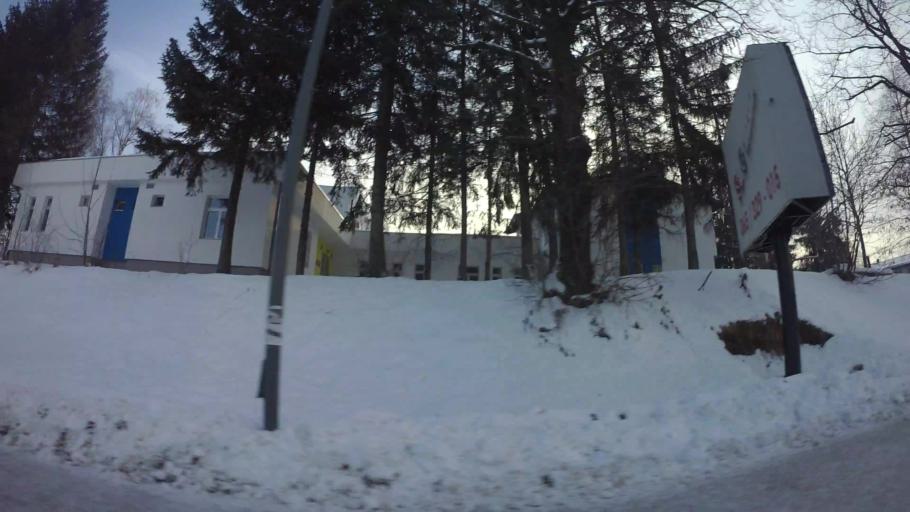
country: BA
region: Federation of Bosnia and Herzegovina
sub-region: Kanton Sarajevo
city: Sarajevo
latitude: 43.8246
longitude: 18.3634
